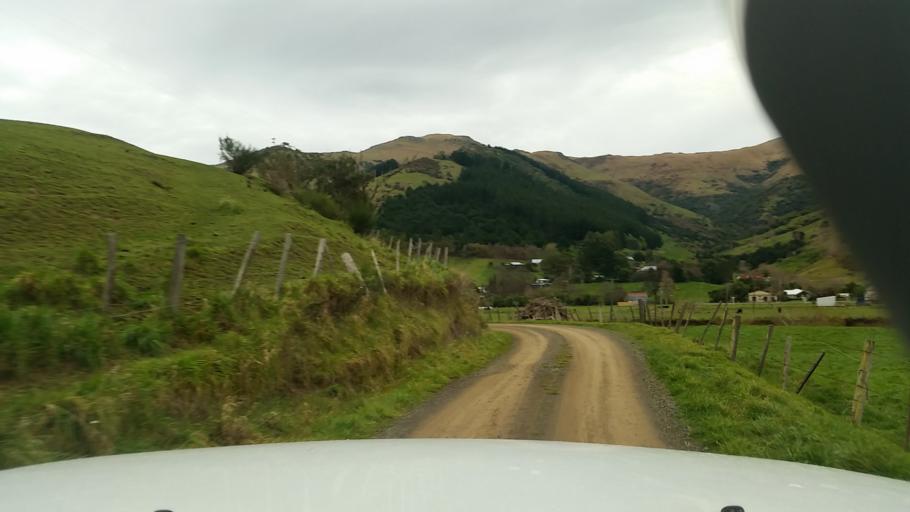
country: NZ
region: Canterbury
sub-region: Christchurch City
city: Christchurch
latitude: -43.7691
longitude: 172.7969
